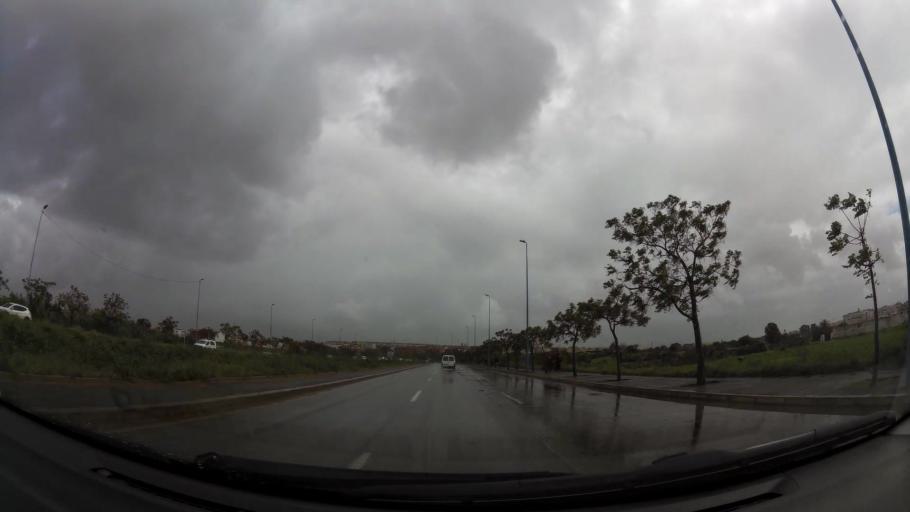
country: MA
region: Grand Casablanca
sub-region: Casablanca
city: Casablanca
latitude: 33.5357
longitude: -7.6588
